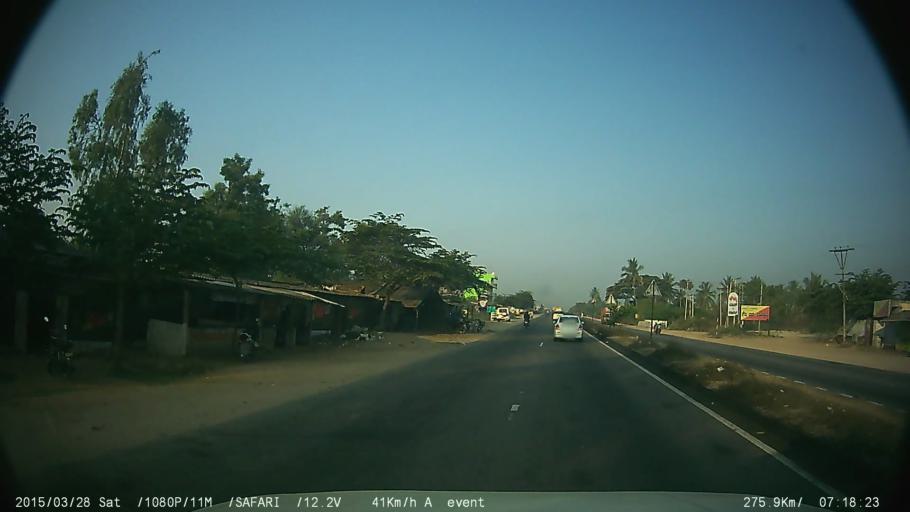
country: IN
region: Karnataka
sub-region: Mandya
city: Mandya
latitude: 12.5027
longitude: 76.8270
